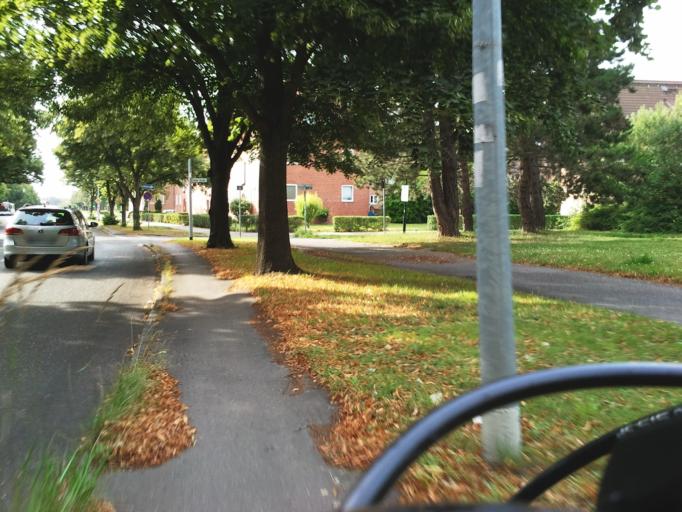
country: DE
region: Mecklenburg-Vorpommern
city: Kritzmow
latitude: 54.0961
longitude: 12.0829
